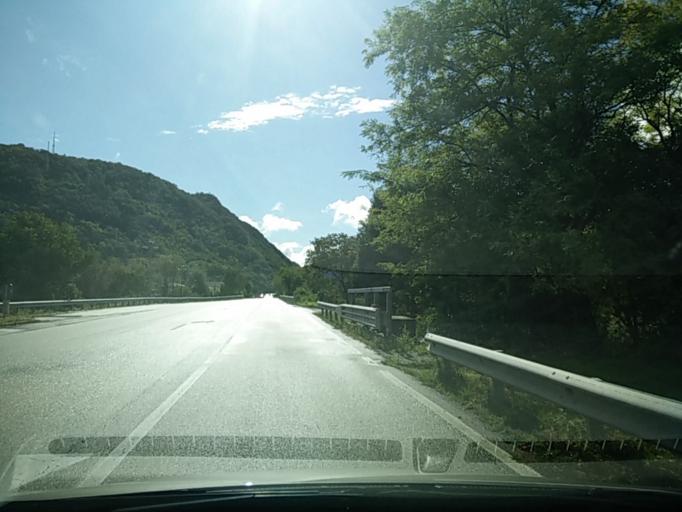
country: IT
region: Veneto
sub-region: Provincia di Treviso
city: Segusino
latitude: 45.9127
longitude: 11.9502
